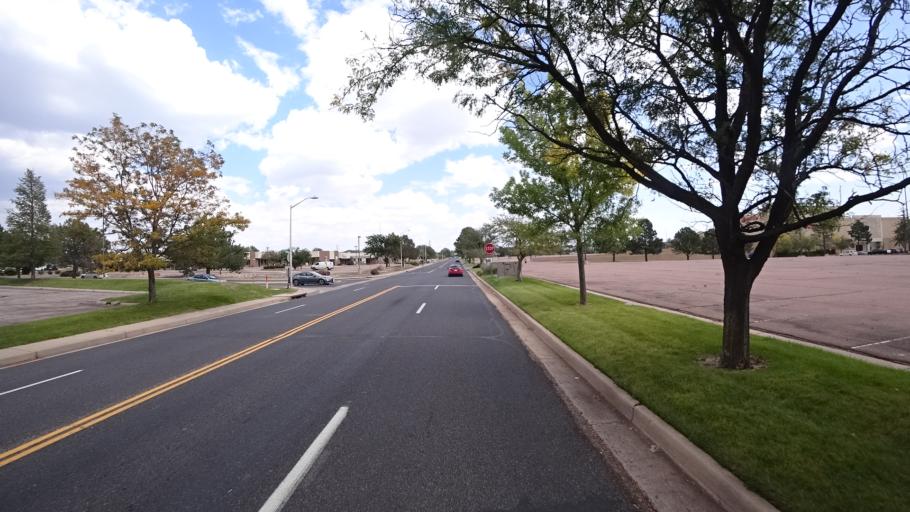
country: US
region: Colorado
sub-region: El Paso County
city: Colorado Springs
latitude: 38.8458
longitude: -104.7631
